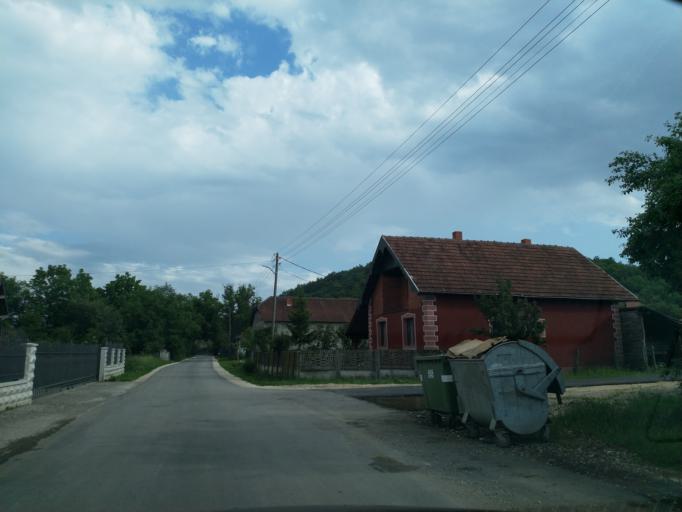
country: RS
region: Central Serbia
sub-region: Borski Okrug
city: Bor
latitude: 44.0177
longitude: 21.9812
